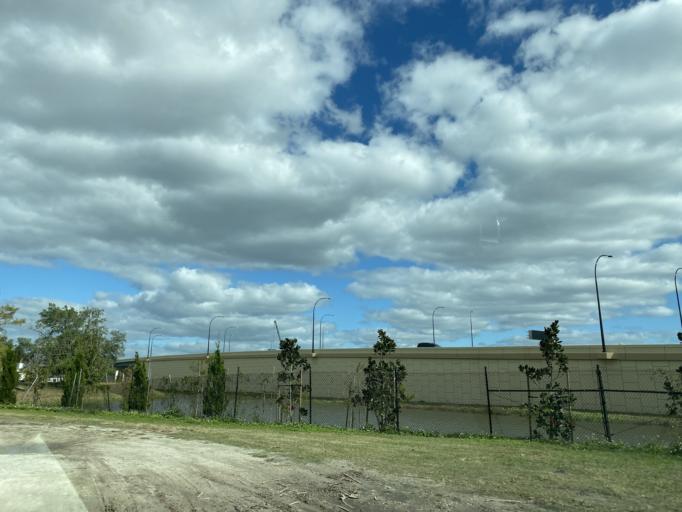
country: US
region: Florida
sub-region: Orange County
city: Holden Heights
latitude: 28.5174
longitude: -81.3888
